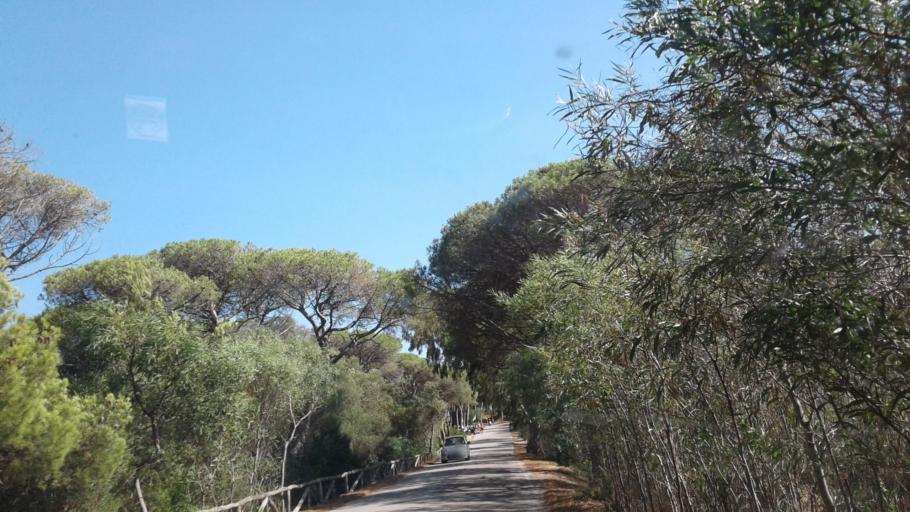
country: IT
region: Sardinia
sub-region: Provincia di Olbia-Tempio
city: La Maddalena
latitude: 41.2127
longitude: 9.4549
